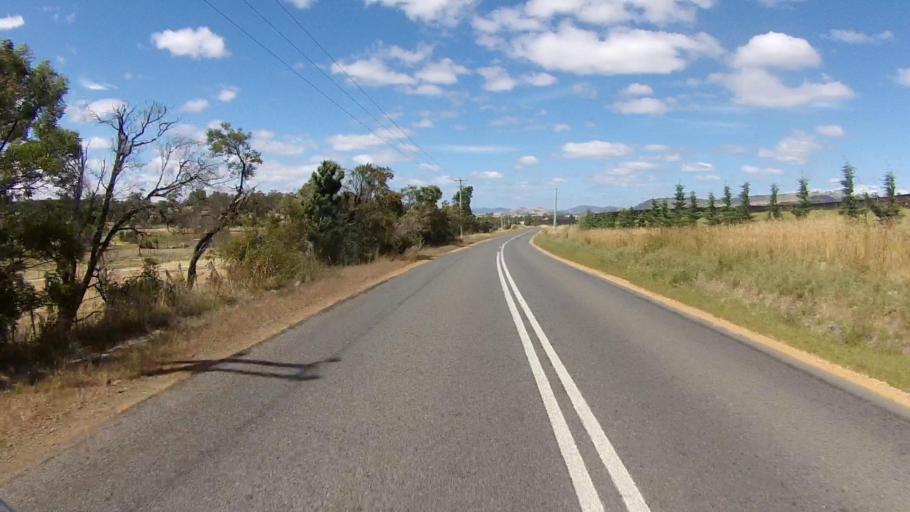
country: AU
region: Tasmania
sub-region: Sorell
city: Sorell
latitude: -42.6441
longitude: 147.4339
